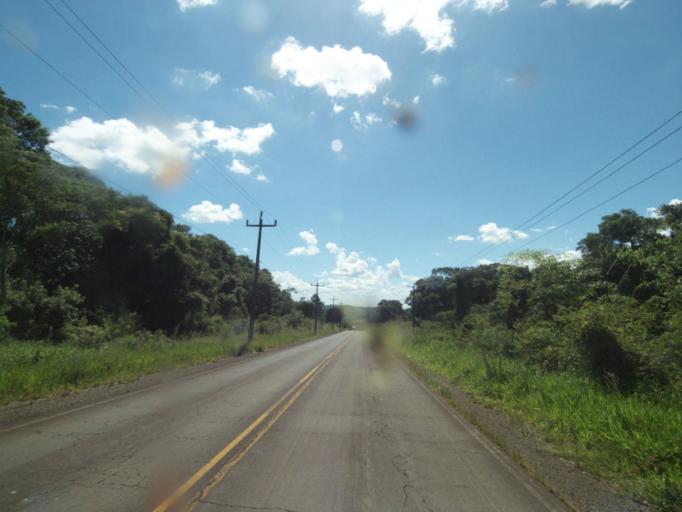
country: BR
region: Parana
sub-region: Chopinzinho
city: Chopinzinho
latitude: -25.7785
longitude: -52.1075
